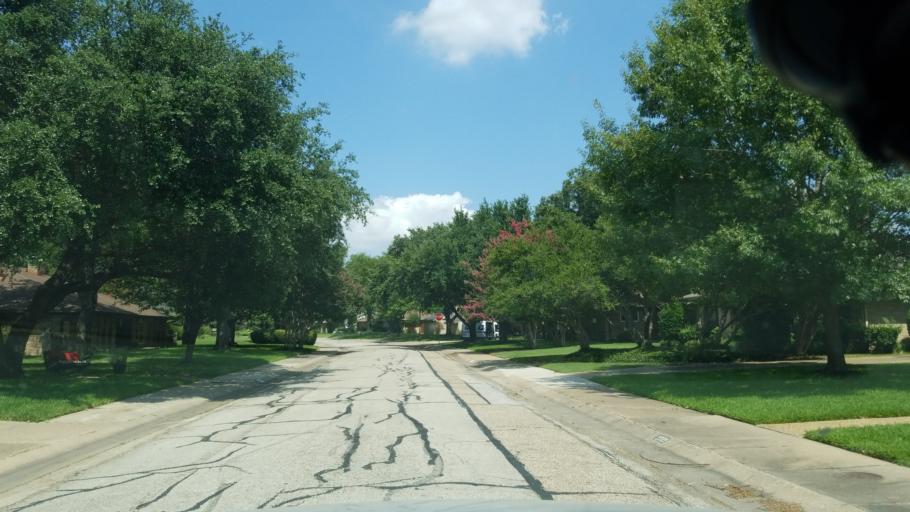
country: US
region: Texas
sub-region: Dallas County
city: Carrollton
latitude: 32.9651
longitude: -96.8608
